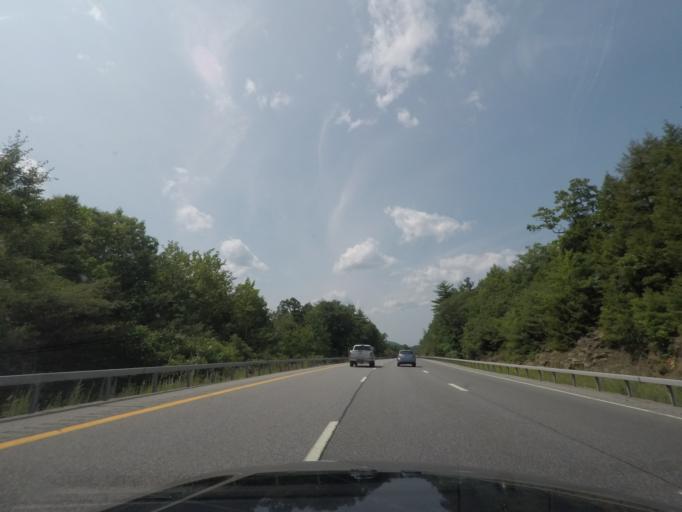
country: US
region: New York
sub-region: Warren County
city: Warrensburg
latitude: 43.4627
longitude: -73.7425
